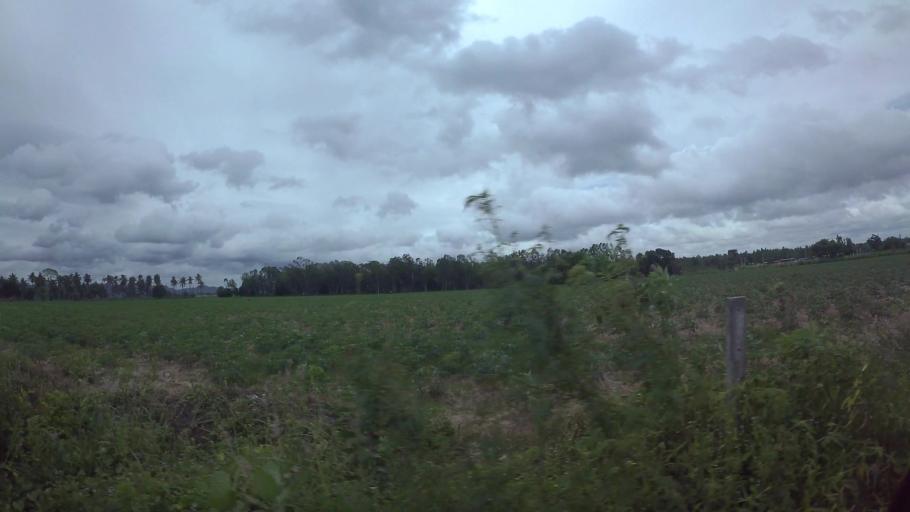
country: TH
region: Chon Buri
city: Si Racha
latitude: 13.1786
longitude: 100.9805
